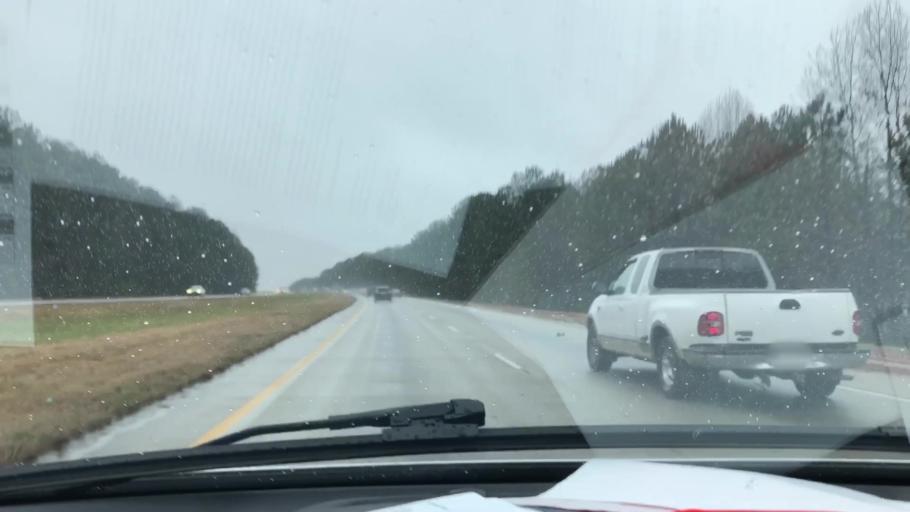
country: US
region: Georgia
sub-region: Gwinnett County
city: Lawrenceville
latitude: 33.9852
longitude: -83.9557
